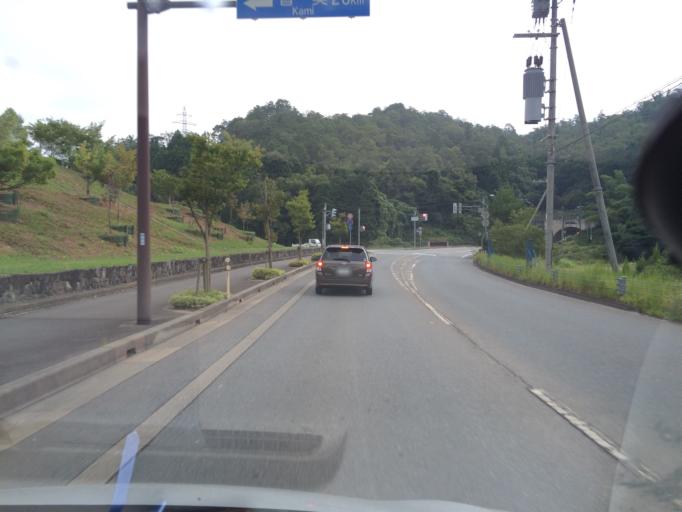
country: JP
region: Hyogo
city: Toyooka
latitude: 35.5257
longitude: 134.8080
